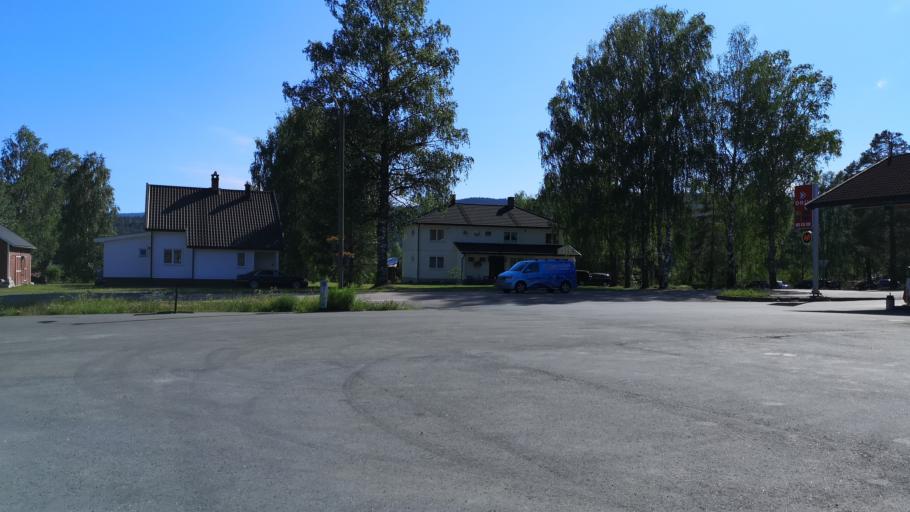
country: NO
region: Buskerud
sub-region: Flesberg
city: Lampeland
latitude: 59.8637
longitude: 9.4301
